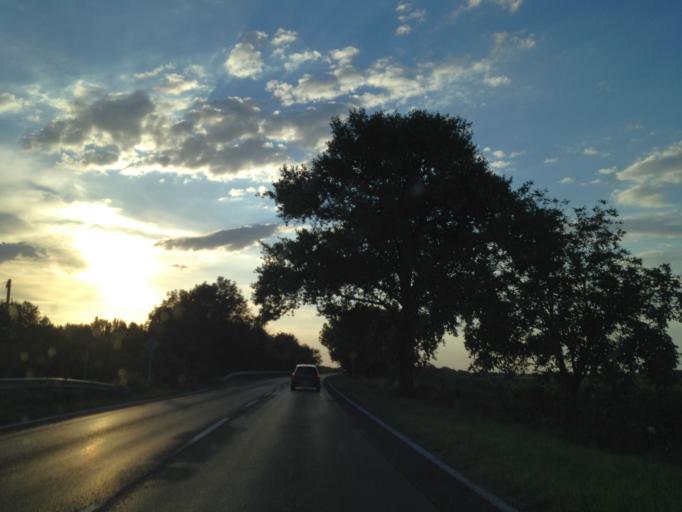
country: HU
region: Gyor-Moson-Sopron
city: Mosonszentmiklos
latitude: 47.7695
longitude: 17.4280
